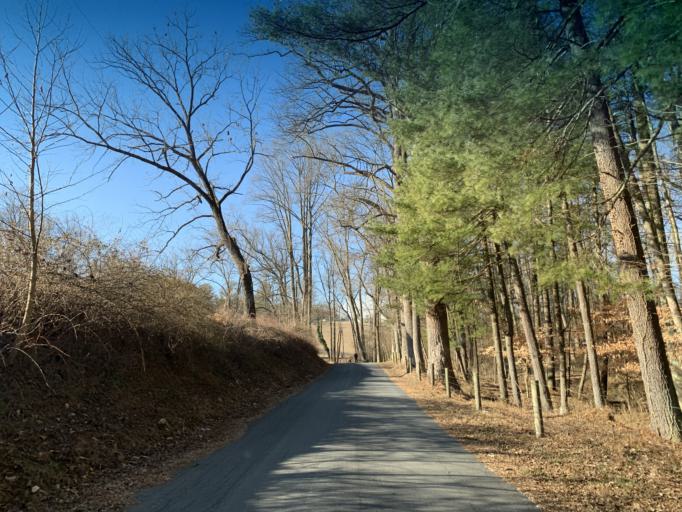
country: US
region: Maryland
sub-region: Harford County
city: Aberdeen
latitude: 39.6124
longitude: -76.2102
